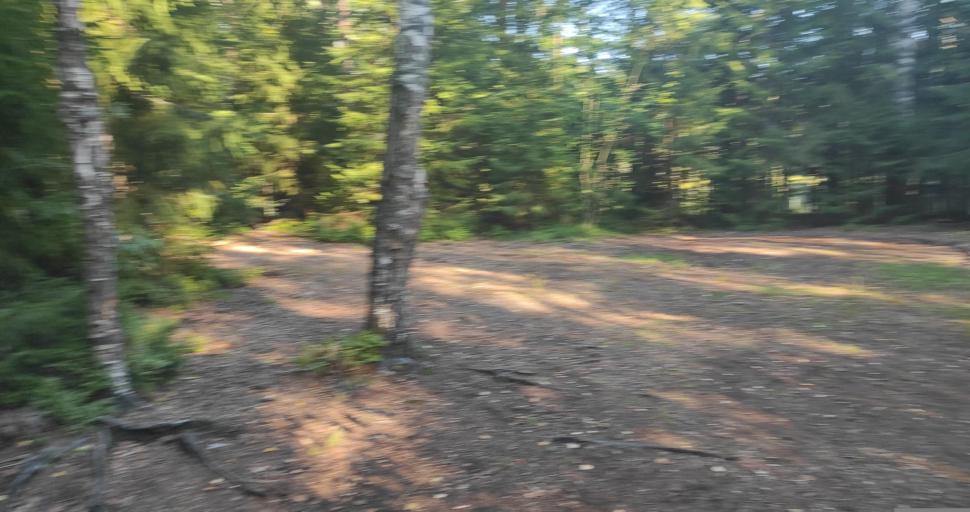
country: RU
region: St.-Petersburg
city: Komarovo
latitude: 60.2253
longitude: 29.7961
